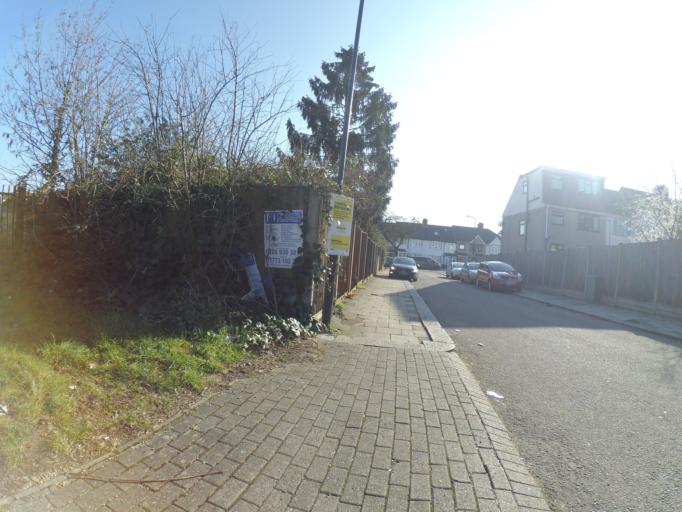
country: GB
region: England
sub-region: Greater London
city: Wembley
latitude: 51.5707
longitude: -0.2654
